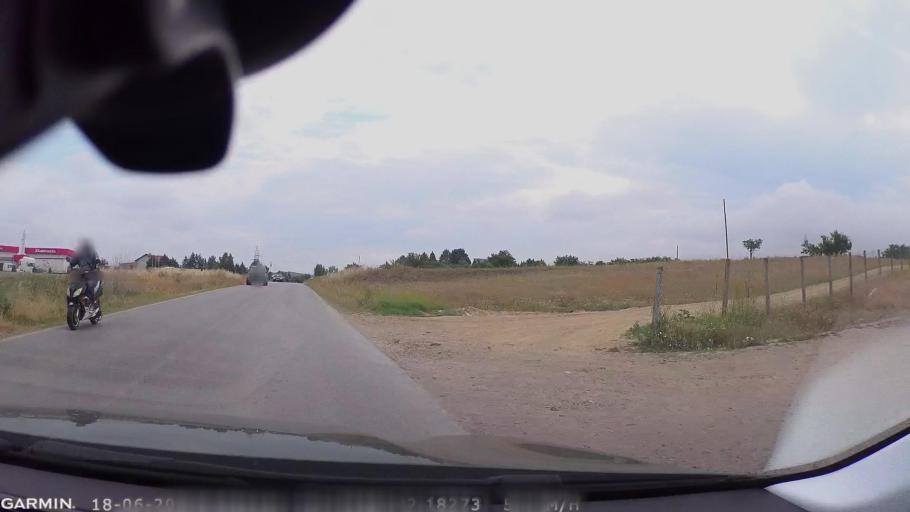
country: MK
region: Stip
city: Shtip
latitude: 41.7742
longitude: 22.1827
